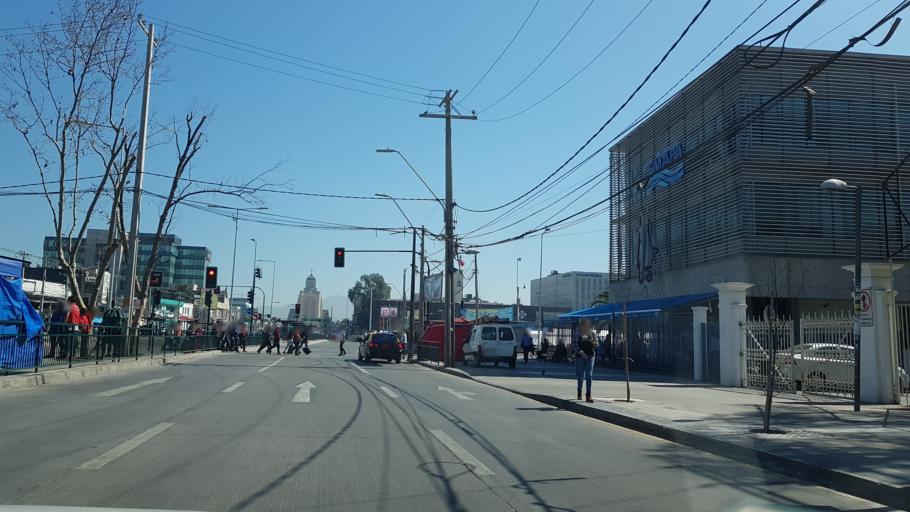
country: CL
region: Santiago Metropolitan
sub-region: Provincia de Santiago
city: Lo Prado
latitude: -33.5105
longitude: -70.7549
